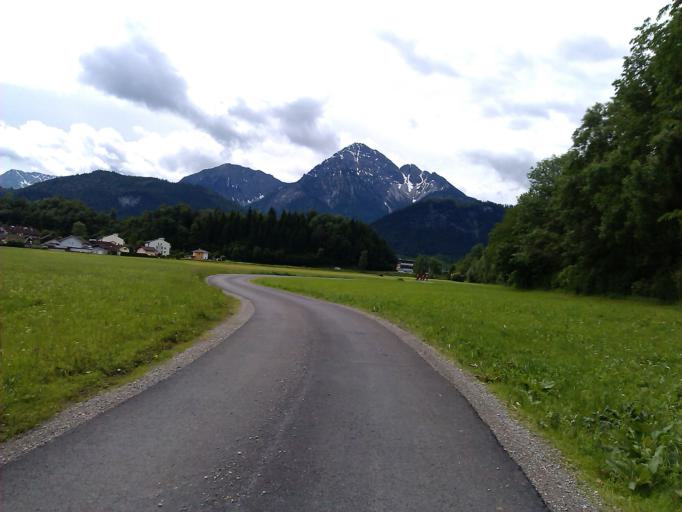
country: AT
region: Tyrol
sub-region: Politischer Bezirk Reutte
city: Lechaschau
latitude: 47.4942
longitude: 10.7112
